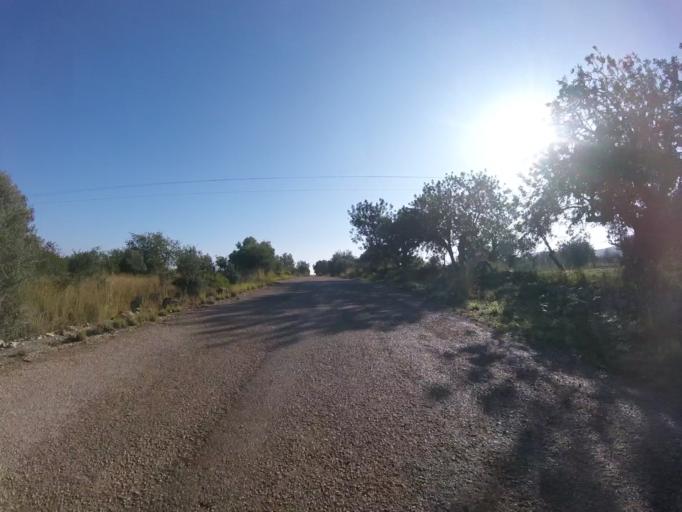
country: ES
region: Valencia
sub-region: Provincia de Castello
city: Peniscola
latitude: 40.3897
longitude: 0.3700
